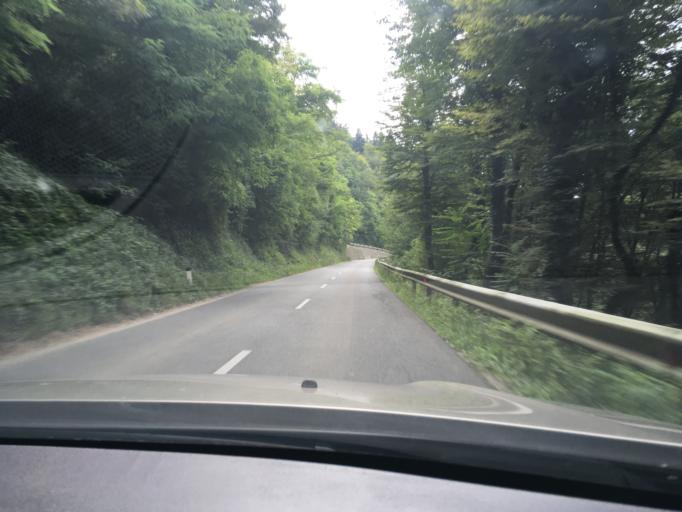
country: SI
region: Dolenjske Toplice
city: Dolenjske Toplice
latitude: 45.7638
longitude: 15.0565
